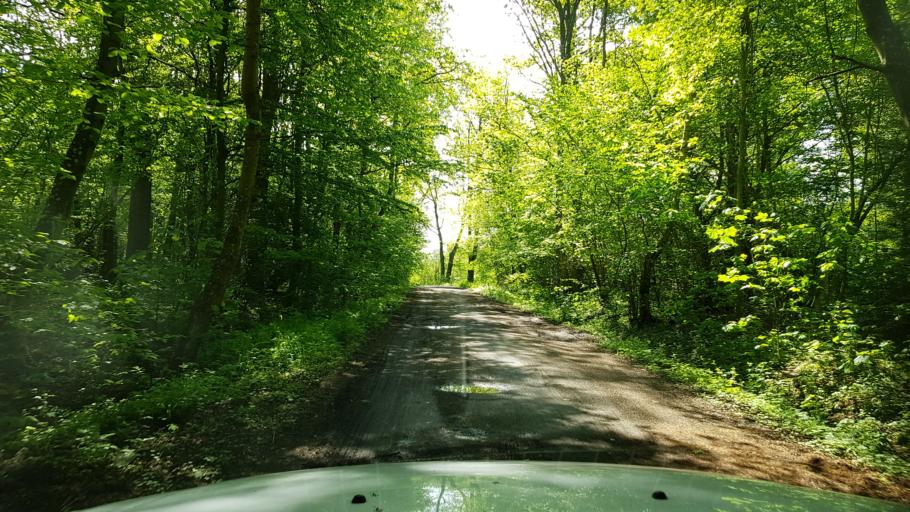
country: PL
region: West Pomeranian Voivodeship
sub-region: Powiat kolobrzeski
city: Ustronie Morskie
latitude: 54.2252
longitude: 15.8097
